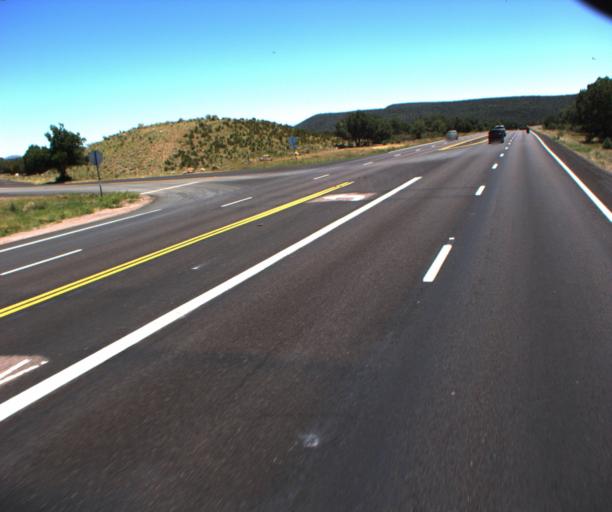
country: US
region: Arizona
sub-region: Gila County
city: Pine
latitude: 34.3326
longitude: -111.4198
